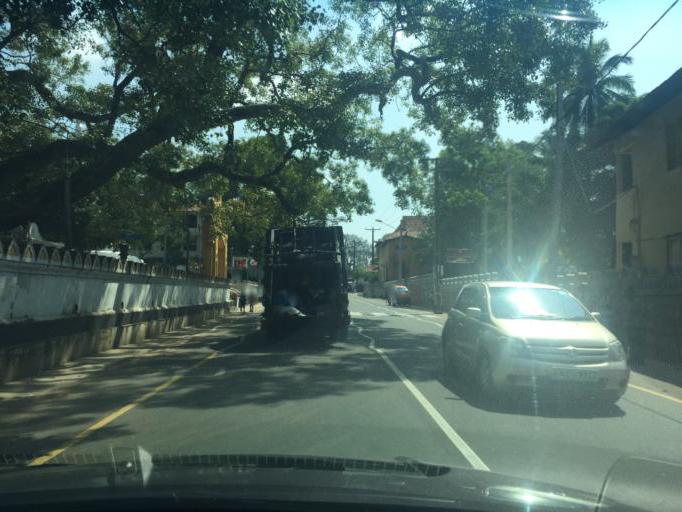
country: LK
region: Western
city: Sri Jayewardenepura Kotte
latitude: 6.8684
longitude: 79.8976
